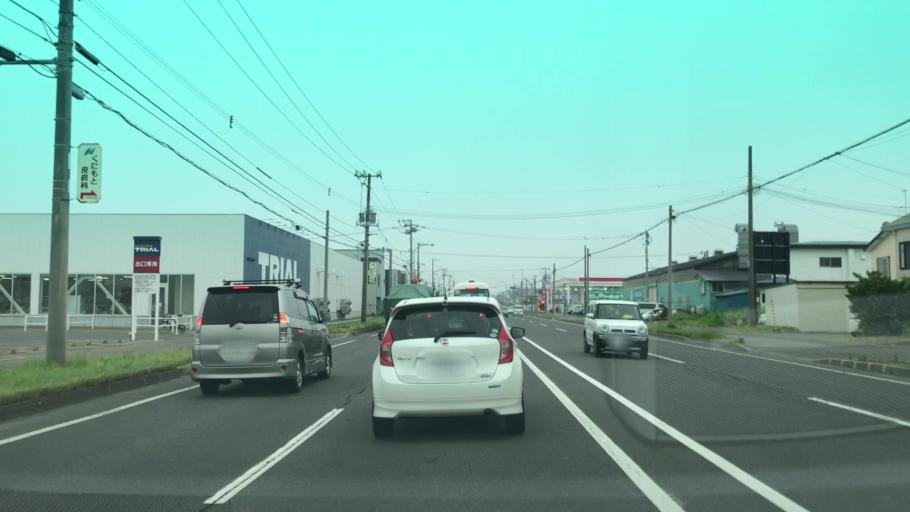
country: JP
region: Hokkaido
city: Muroran
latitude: 42.3801
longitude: 141.0727
